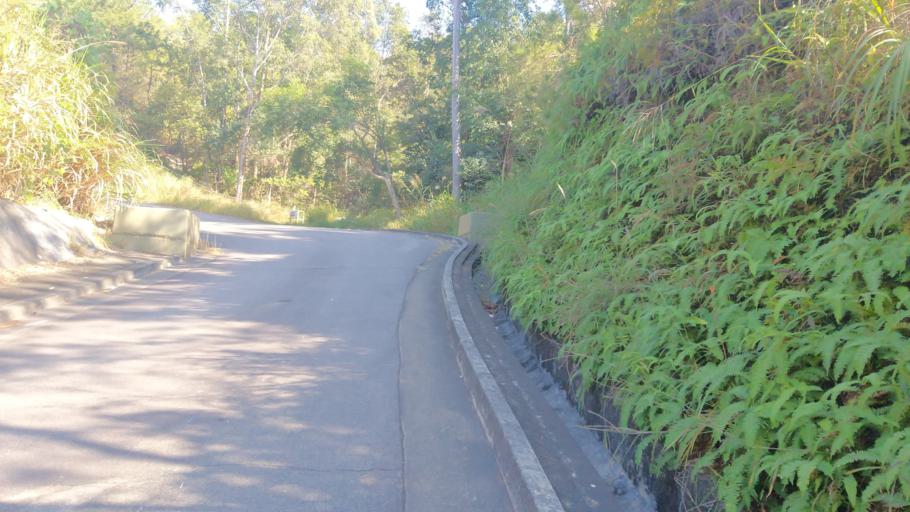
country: HK
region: Tuen Mun
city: Tuen Mun
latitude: 22.4060
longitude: 113.9874
